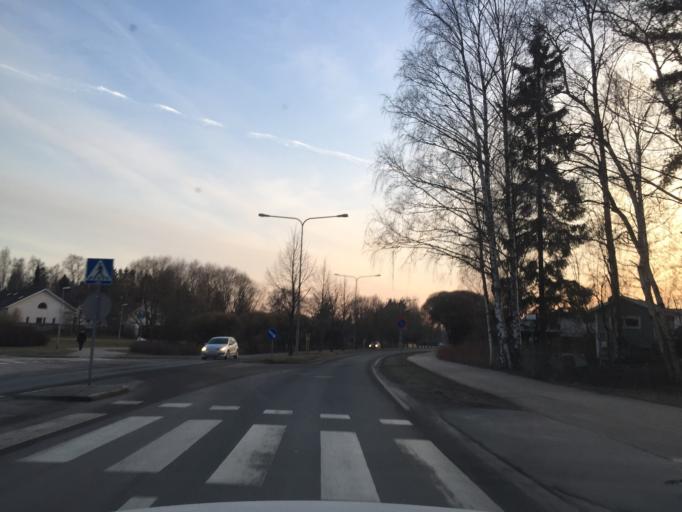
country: FI
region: Uusimaa
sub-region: Helsinki
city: Vantaa
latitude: 60.2573
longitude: 24.9863
